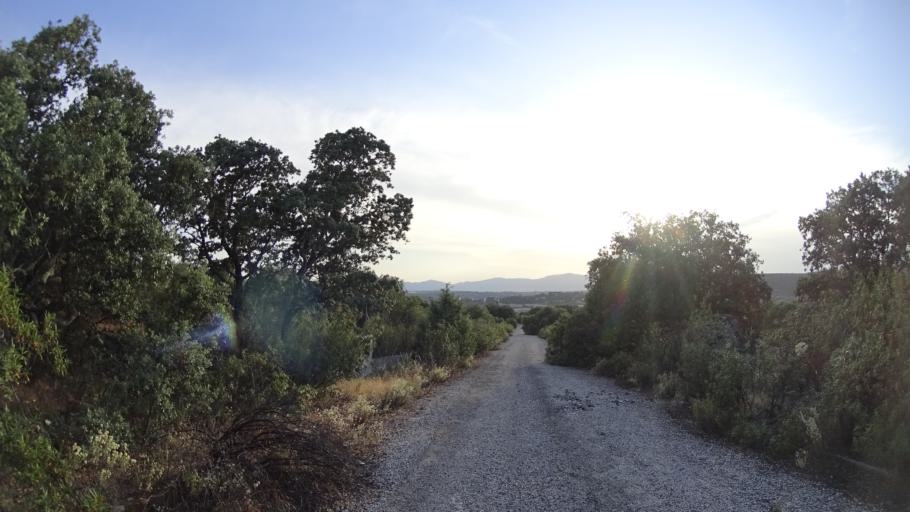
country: ES
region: Madrid
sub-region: Provincia de Madrid
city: Torrelodones
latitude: 40.5942
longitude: -3.9441
